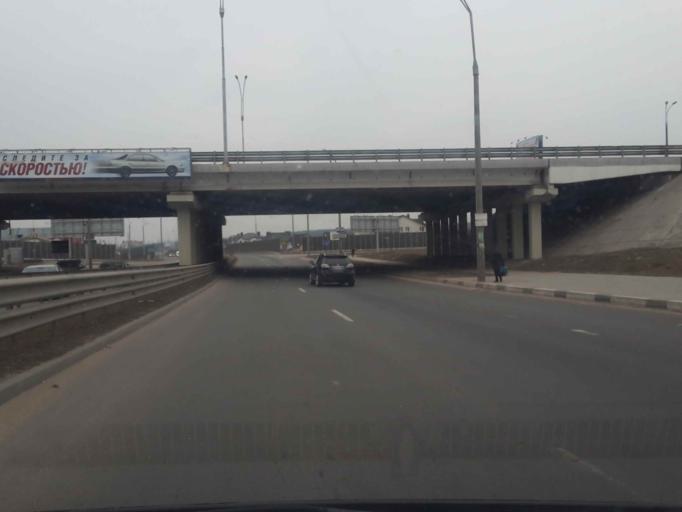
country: BY
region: Minsk
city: Bal'shavik
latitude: 53.9689
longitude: 27.5385
